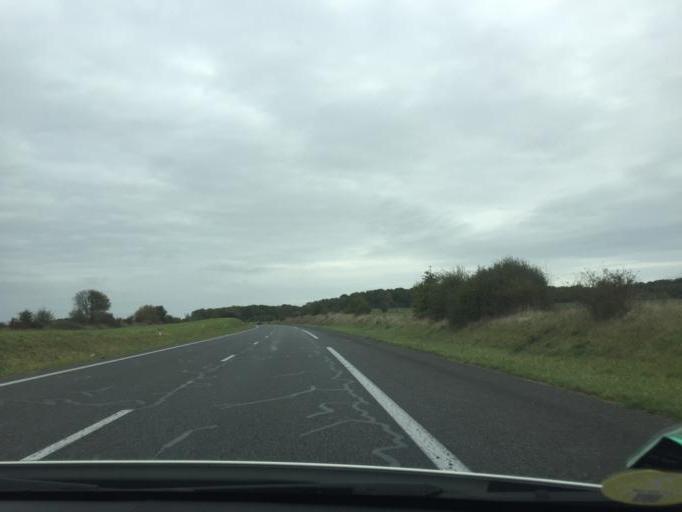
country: FR
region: Bourgogne
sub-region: Departement de l'Yonne
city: Egriselles-le-Bocage
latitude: 48.0929
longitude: 3.1369
